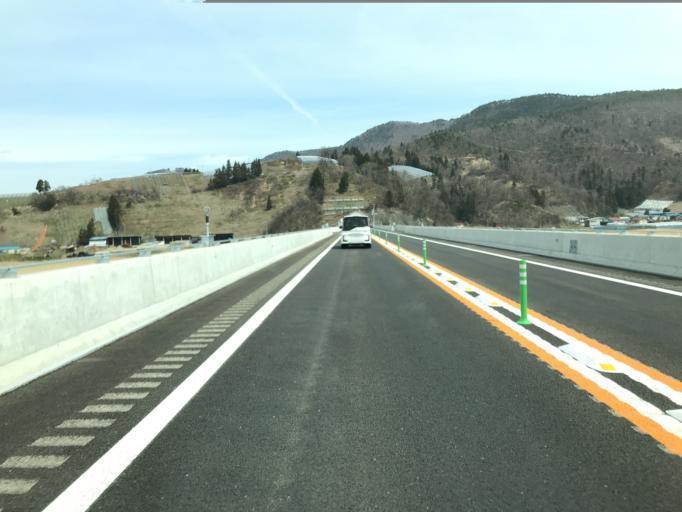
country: JP
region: Yamagata
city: Takahata
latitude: 38.0395
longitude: 140.1876
